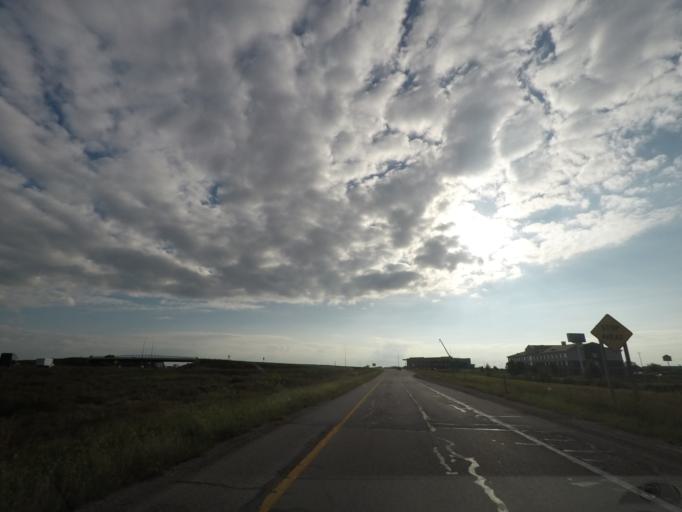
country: US
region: Iowa
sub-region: Polk County
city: Altoona
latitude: 41.6657
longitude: -93.4678
